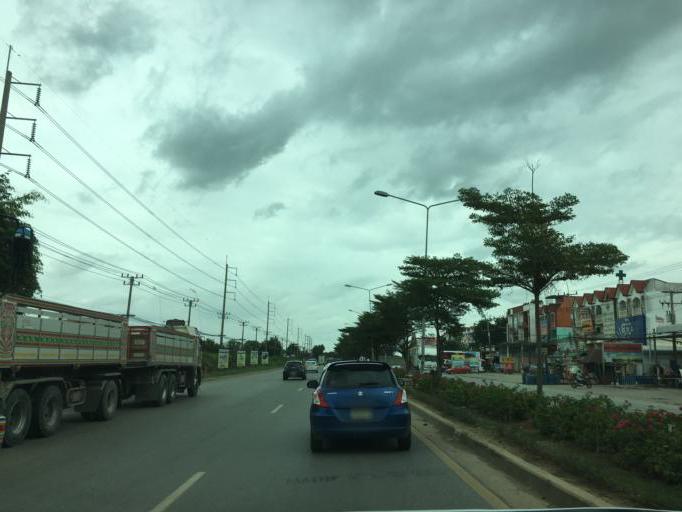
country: TH
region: Phra Nakhon Si Ayutthaya
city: Wang Noi
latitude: 14.2742
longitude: 100.6828
